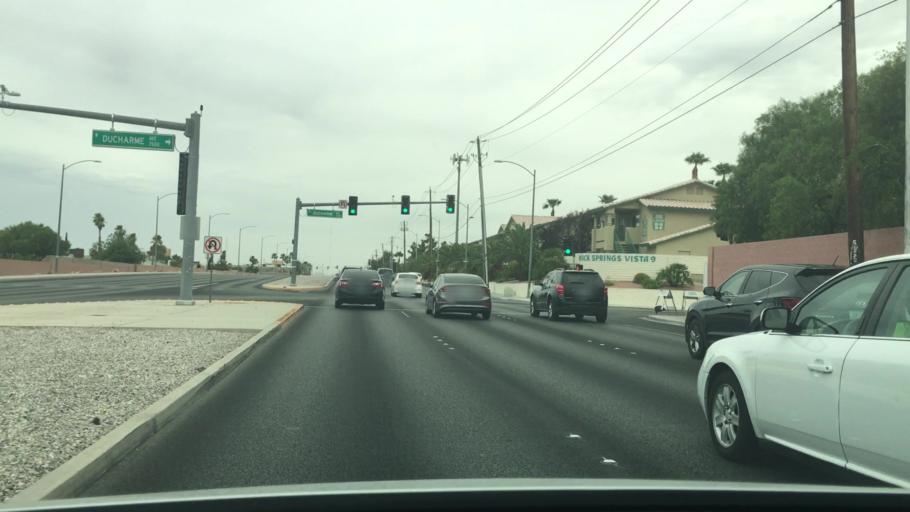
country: US
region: Nevada
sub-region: Clark County
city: Spring Valley
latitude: 36.1706
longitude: -115.2600
